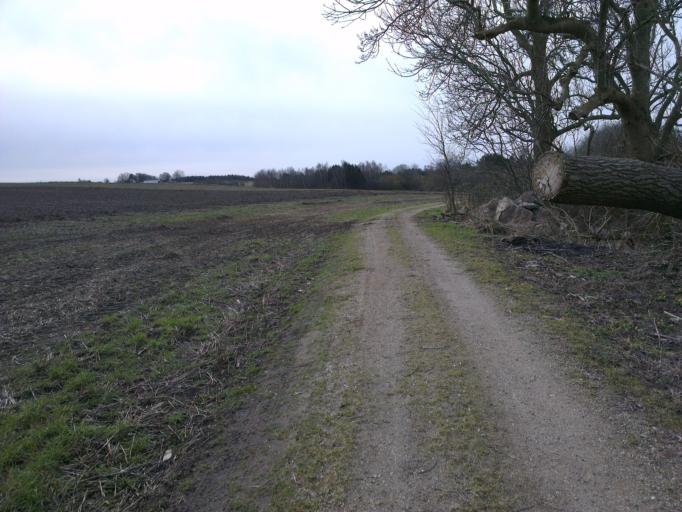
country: DK
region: Zealand
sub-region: Lejre Kommune
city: Ejby
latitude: 55.7756
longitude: 11.8621
